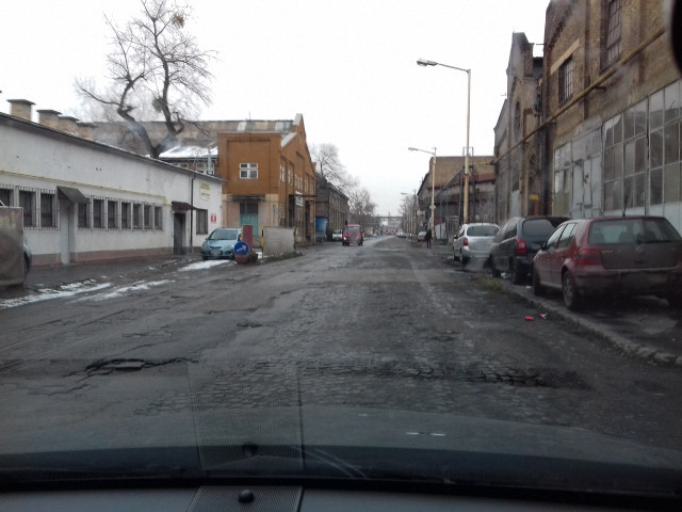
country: HU
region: Budapest
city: Budapest XXI. keruelet
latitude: 47.4311
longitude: 19.0615
